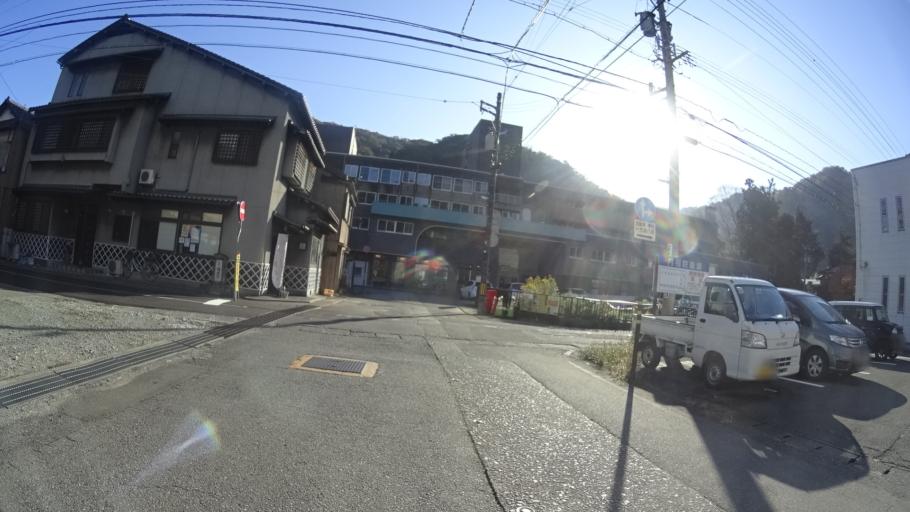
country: JP
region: Fukui
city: Maruoka
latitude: 36.2467
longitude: 136.3750
